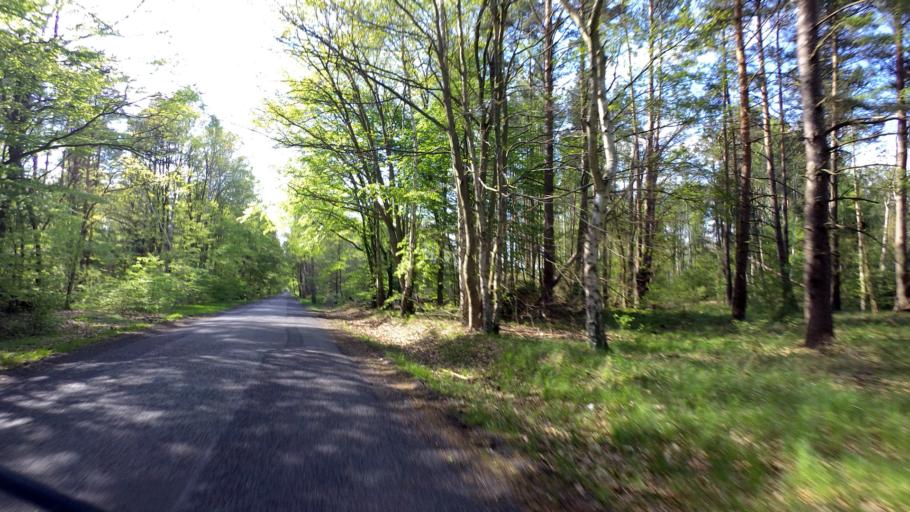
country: DE
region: Brandenburg
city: Templin
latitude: 53.0075
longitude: 13.4583
